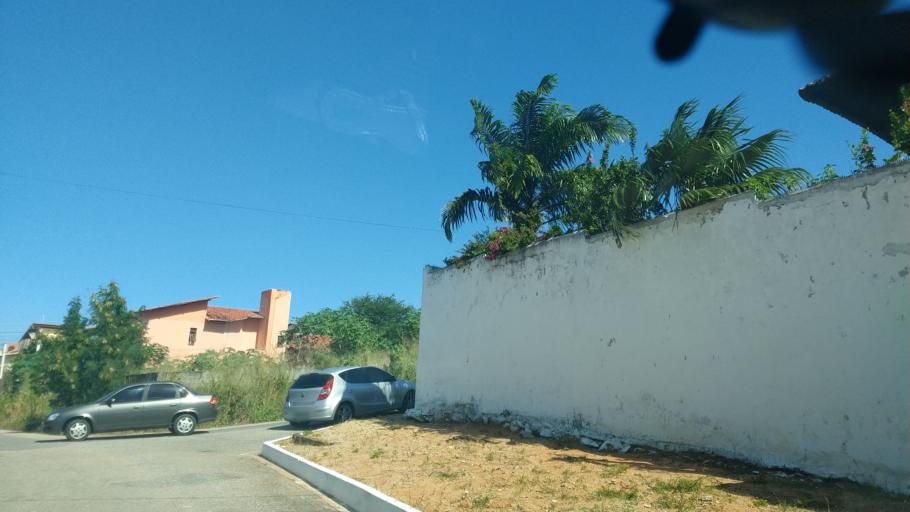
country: BR
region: Rio Grande do Norte
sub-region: Natal
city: Natal
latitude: -5.8448
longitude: -35.2049
